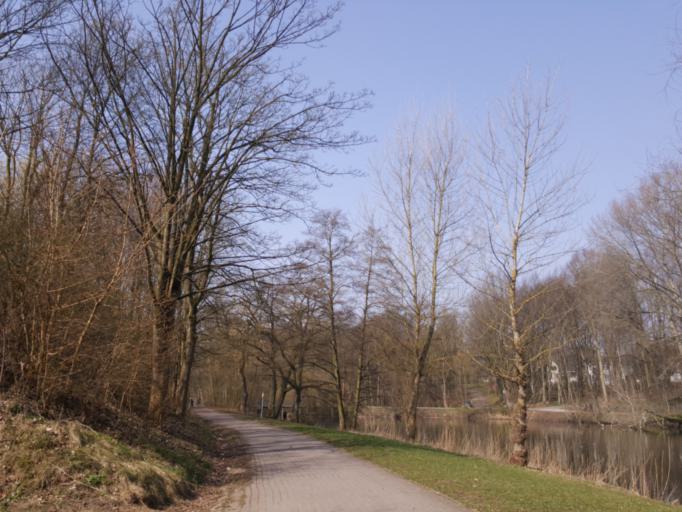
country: DE
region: Schleswig-Holstein
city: Oststeinbek
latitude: 53.5357
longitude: 10.1482
